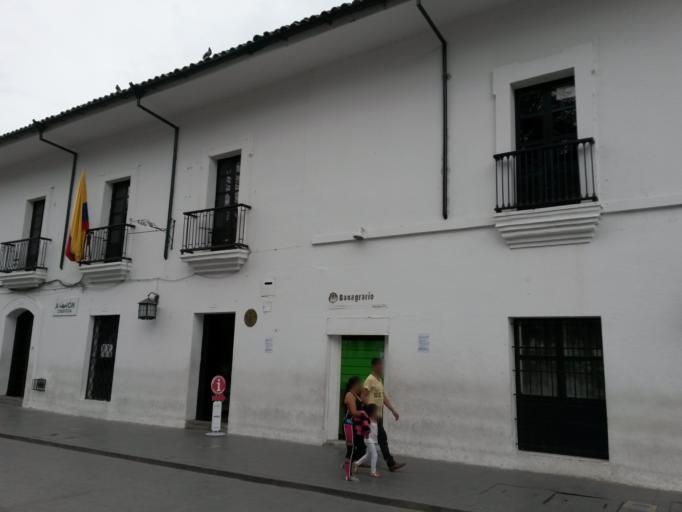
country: CO
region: Cauca
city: Popayan
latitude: 2.4423
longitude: -76.6066
